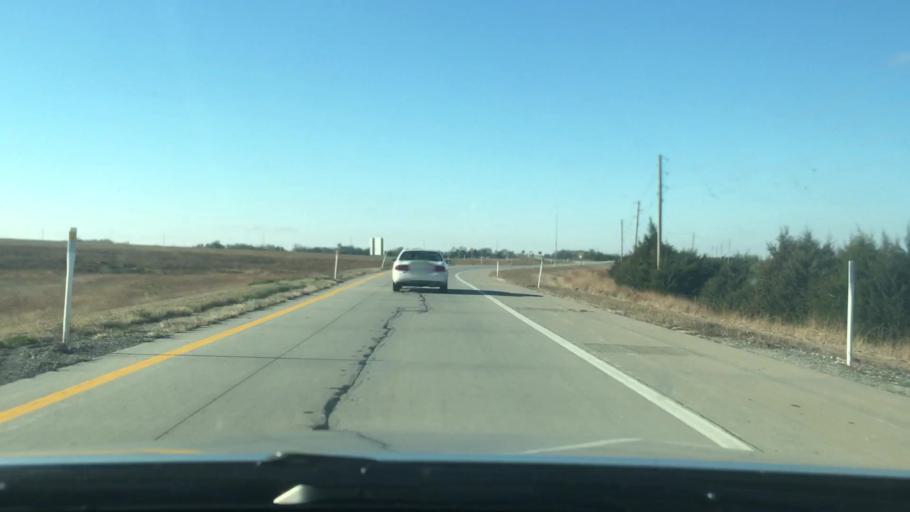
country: US
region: Kansas
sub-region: Reno County
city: South Hutchinson
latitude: 38.0163
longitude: -97.9667
